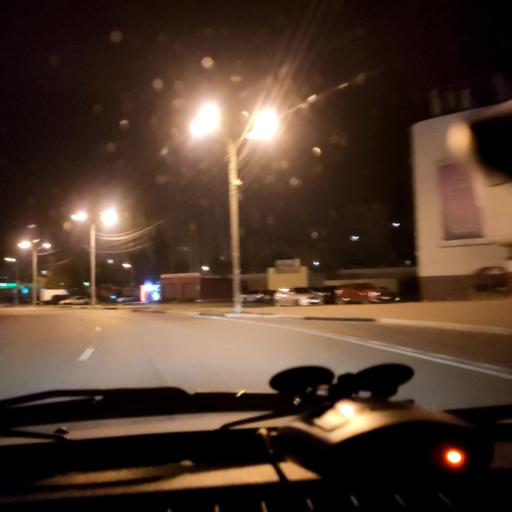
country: RU
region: Voronezj
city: Podgornoye
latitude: 51.7158
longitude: 39.1716
